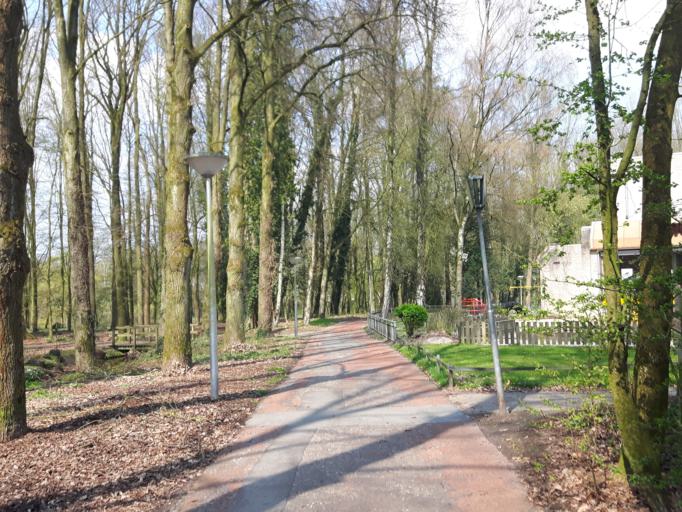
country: NL
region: Overijssel
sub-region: Gemeente Enschede
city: Enschede
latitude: 52.1928
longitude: 6.8522
